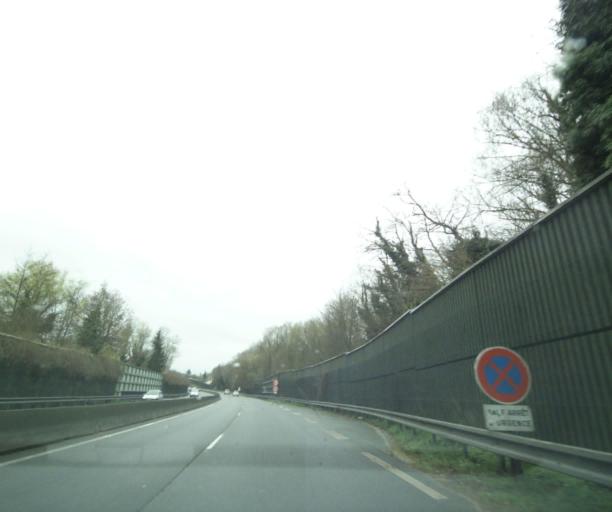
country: FR
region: Ile-de-France
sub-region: Departement de l'Essonne
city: Arpajon
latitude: 48.5896
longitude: 2.2367
